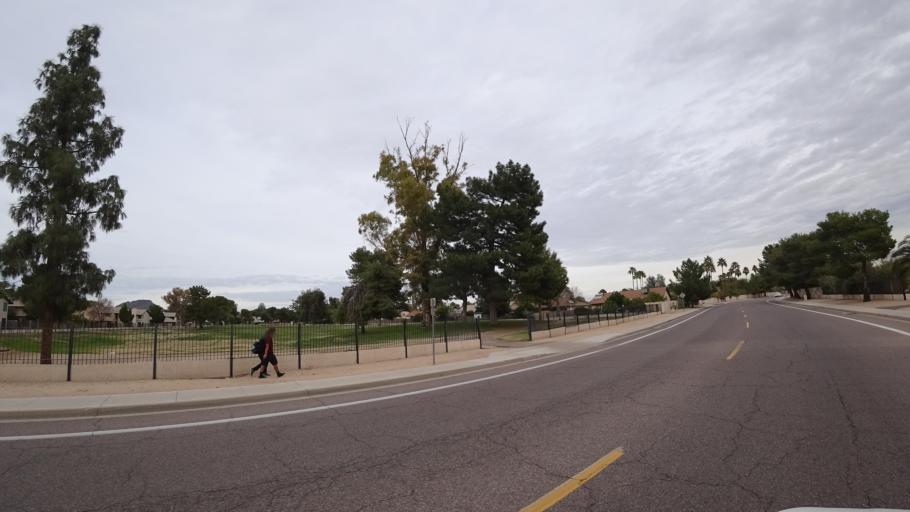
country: US
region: Arizona
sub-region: Maricopa County
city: Peoria
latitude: 33.6469
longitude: -112.1561
